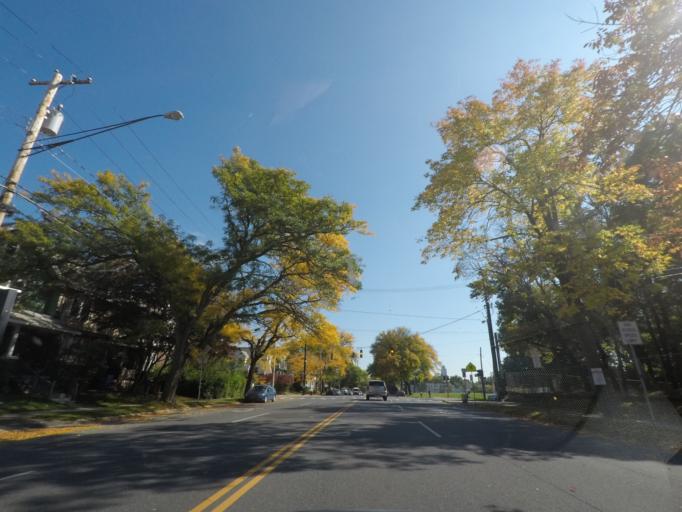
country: US
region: New York
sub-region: Albany County
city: West Albany
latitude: 42.6664
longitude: -73.7801
